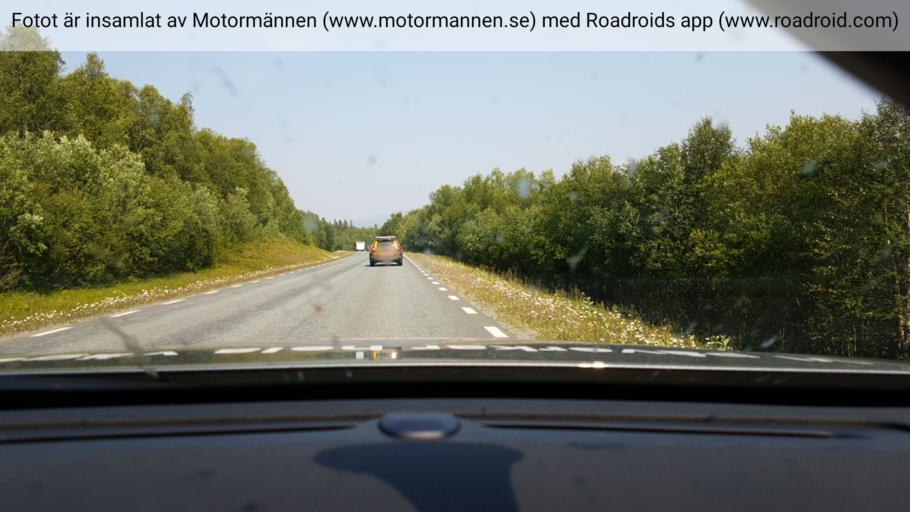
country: NO
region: Nordland
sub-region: Rana
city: Mo i Rana
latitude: 65.7658
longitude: 15.1142
